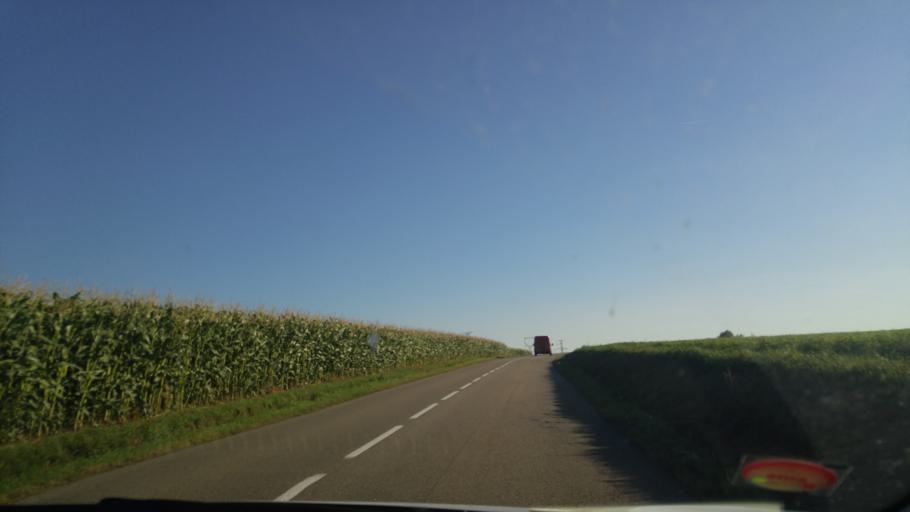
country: CZ
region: South Moravian
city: Ricany
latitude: 49.2246
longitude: 16.4167
